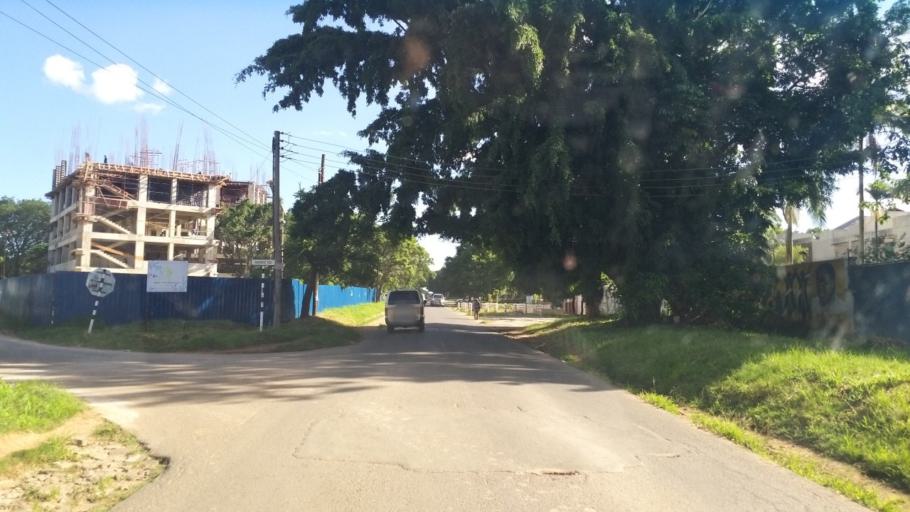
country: ZM
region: Lusaka
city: Lusaka
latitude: -15.4193
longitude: 28.3126
